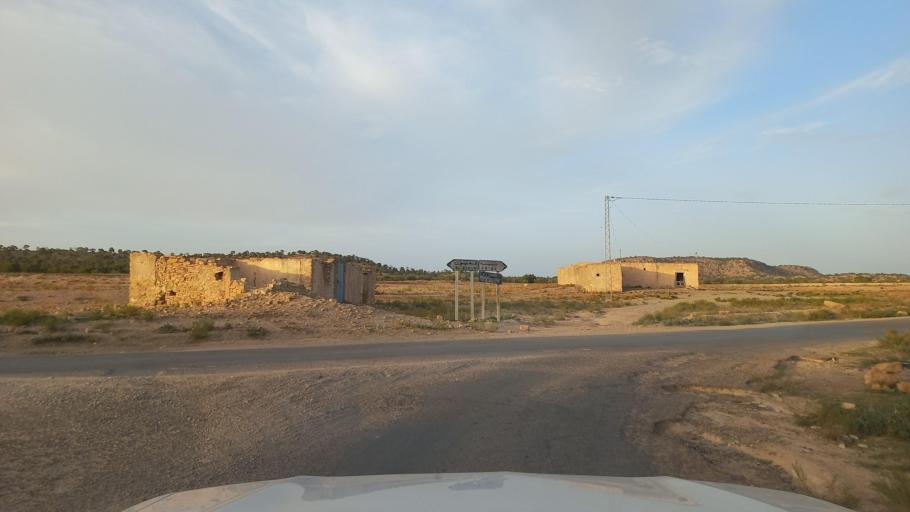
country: TN
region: Al Qasrayn
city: Sbiba
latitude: 35.4138
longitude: 8.9278
